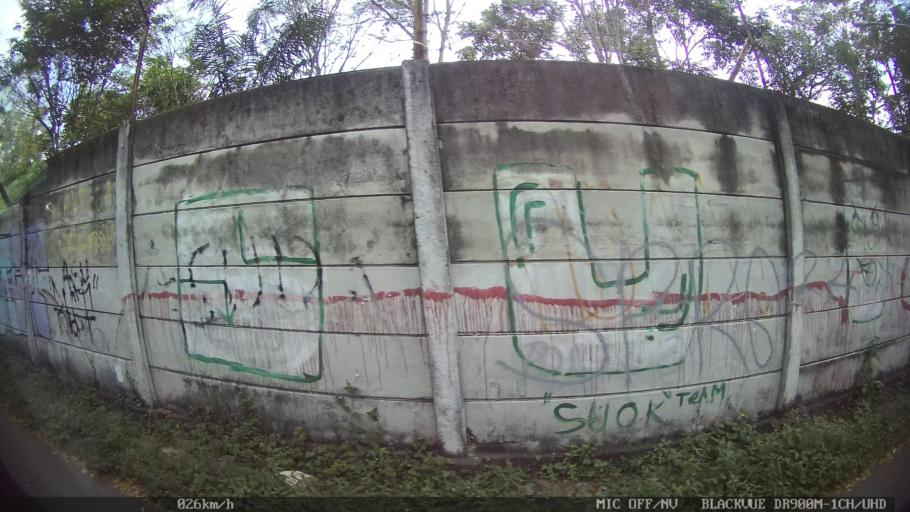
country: ID
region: Daerah Istimewa Yogyakarta
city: Yogyakarta
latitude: -7.7651
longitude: 110.3563
